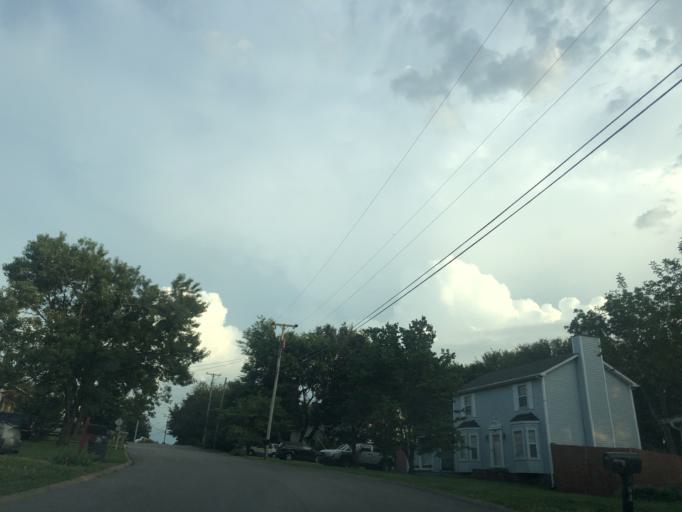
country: US
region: Tennessee
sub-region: Davidson County
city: Lakewood
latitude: 36.1394
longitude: -86.6330
